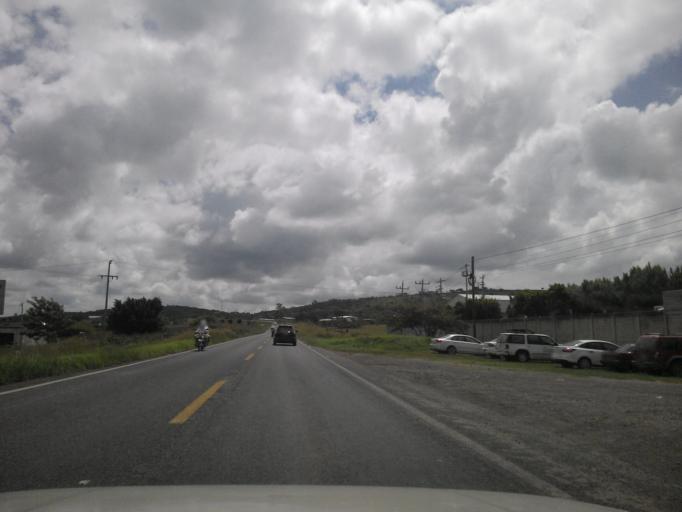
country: MX
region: Jalisco
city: Zapotlanejo
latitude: 20.6042
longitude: -102.9791
